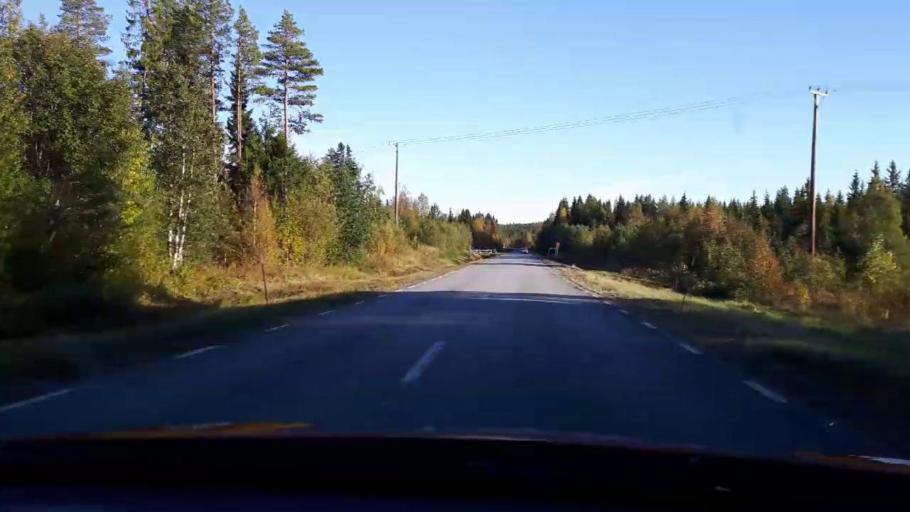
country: SE
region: Jaemtland
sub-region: OEstersunds Kommun
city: Lit
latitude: 63.7409
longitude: 14.7350
